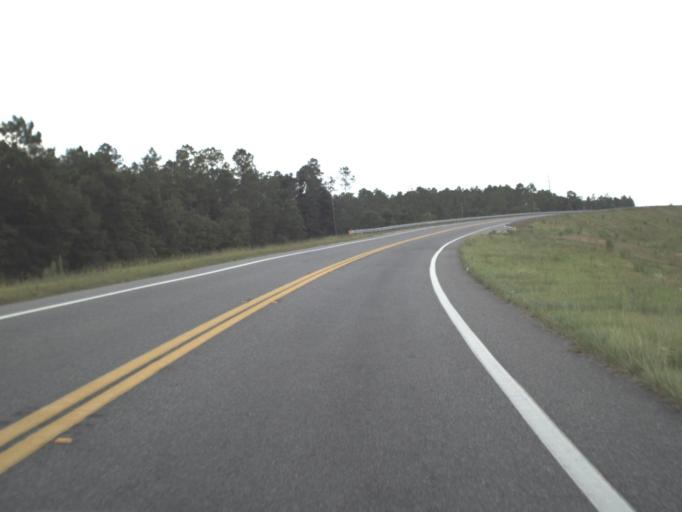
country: US
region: Florida
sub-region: Madison County
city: Madison
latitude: 30.3938
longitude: -83.2035
